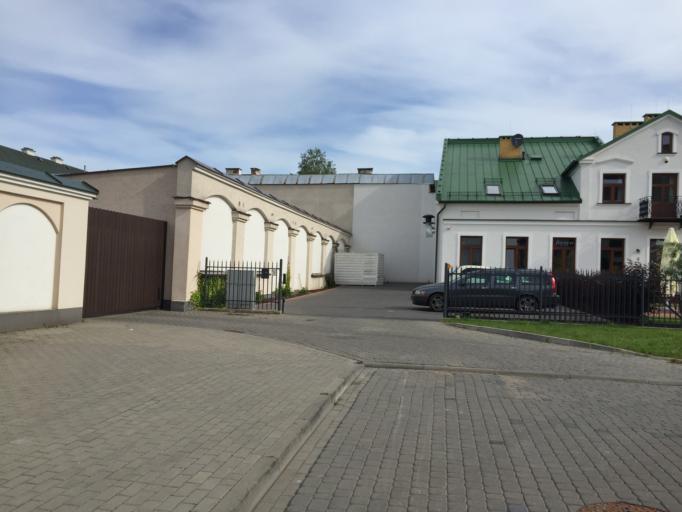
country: PL
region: Podlasie
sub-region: Suwalki
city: Suwalki
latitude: 54.1005
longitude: 22.9294
